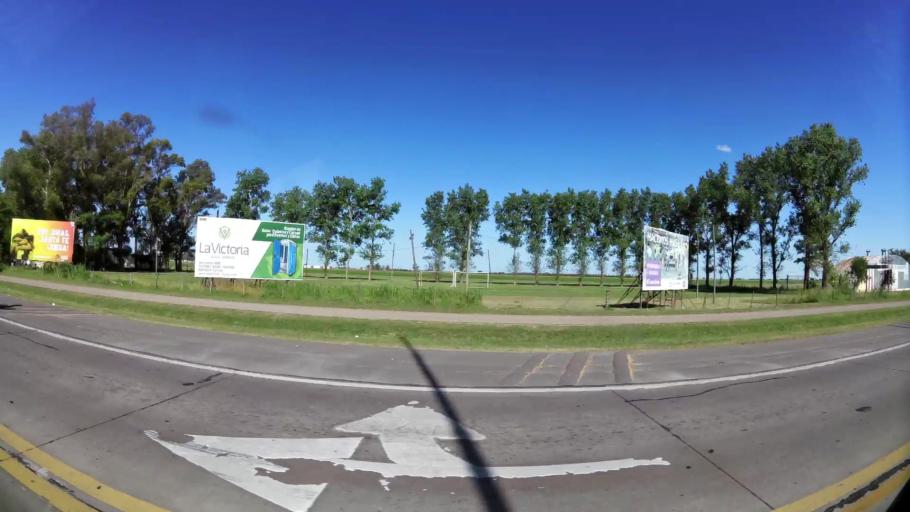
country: AR
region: Santa Fe
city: Rafaela
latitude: -31.2806
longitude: -61.5124
